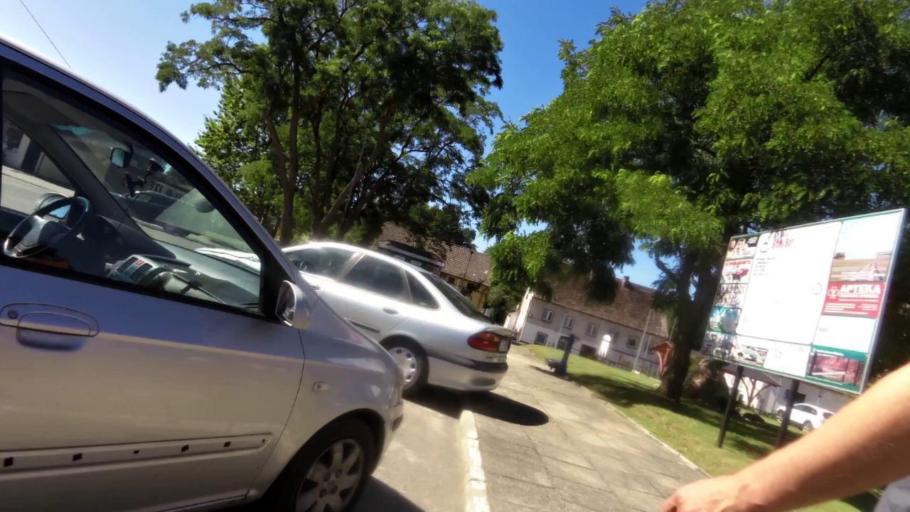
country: PL
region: West Pomeranian Voivodeship
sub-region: Powiat szczecinecki
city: Bialy Bor
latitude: 53.8968
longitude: 16.8348
